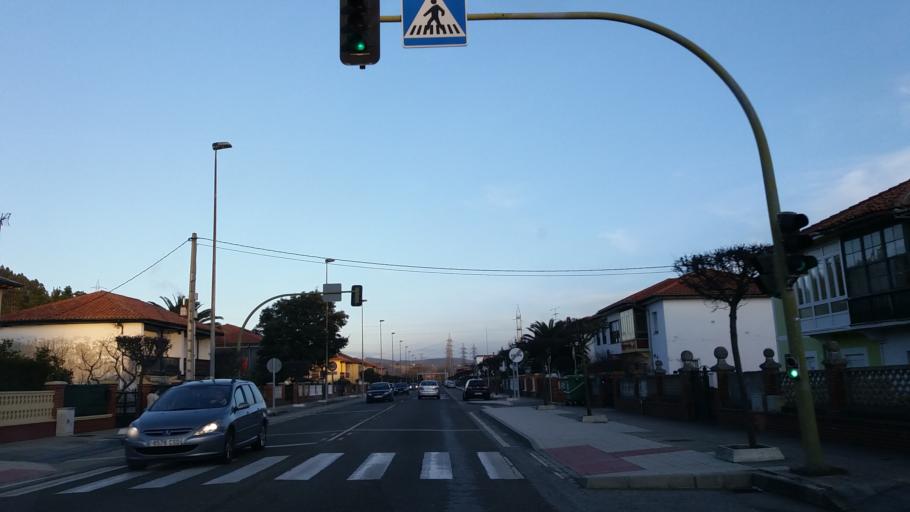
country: ES
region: Cantabria
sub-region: Provincia de Cantabria
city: Reocin
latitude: 43.3578
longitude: -4.0828
